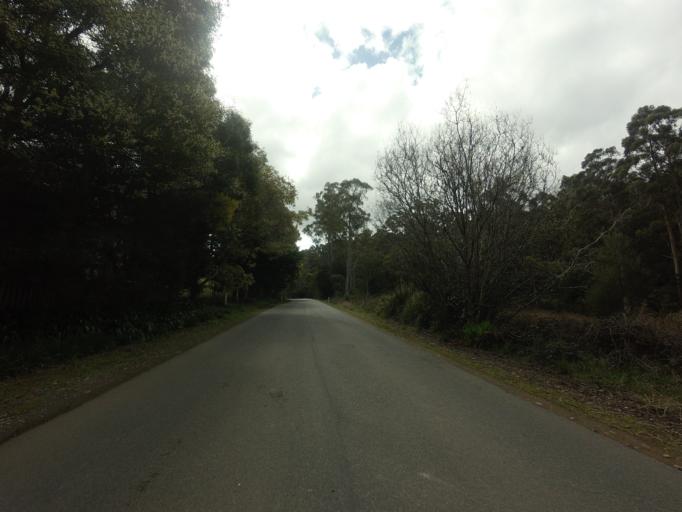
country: AU
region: Tasmania
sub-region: Huon Valley
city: Geeveston
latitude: -43.4168
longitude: 146.9647
